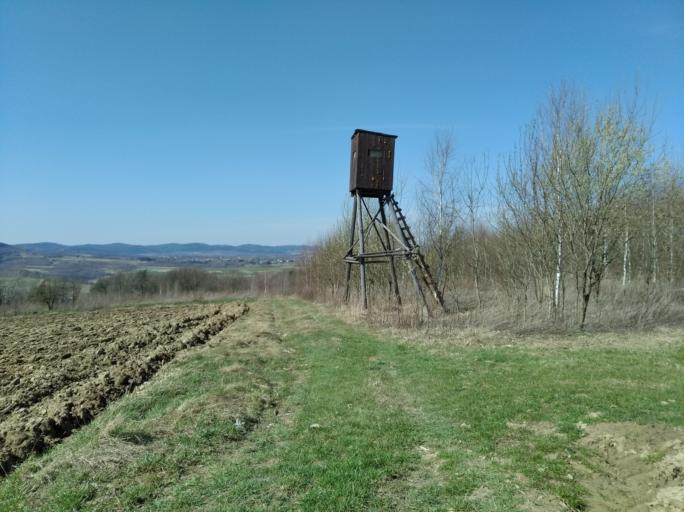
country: PL
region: Subcarpathian Voivodeship
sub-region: Powiat strzyzowski
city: Strzyzow
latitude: 49.8532
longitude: 21.8223
